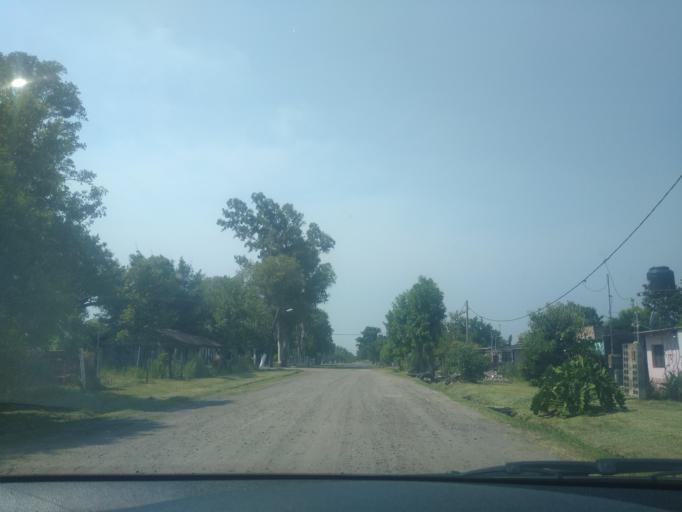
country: AR
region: Chaco
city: Puerto Tirol
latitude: -27.5623
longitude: -59.3049
